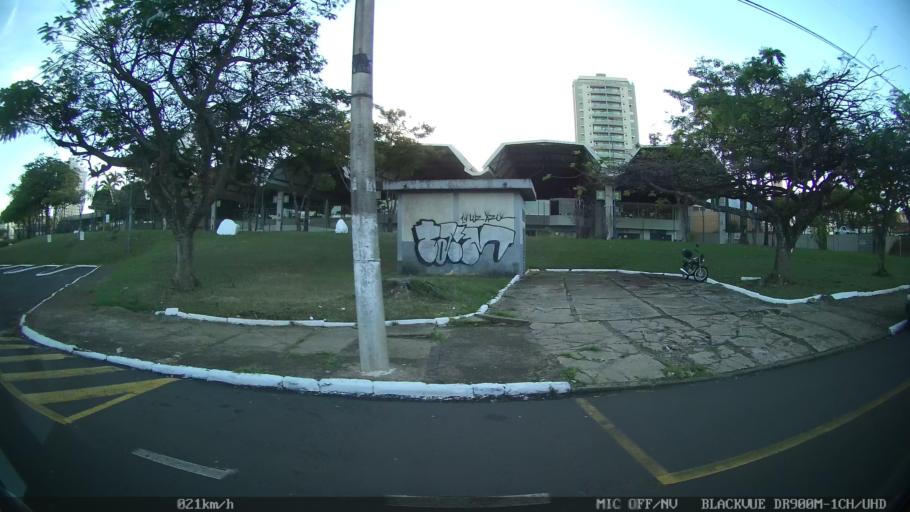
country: BR
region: Sao Paulo
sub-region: Franca
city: Franca
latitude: -20.5321
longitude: -47.3889
